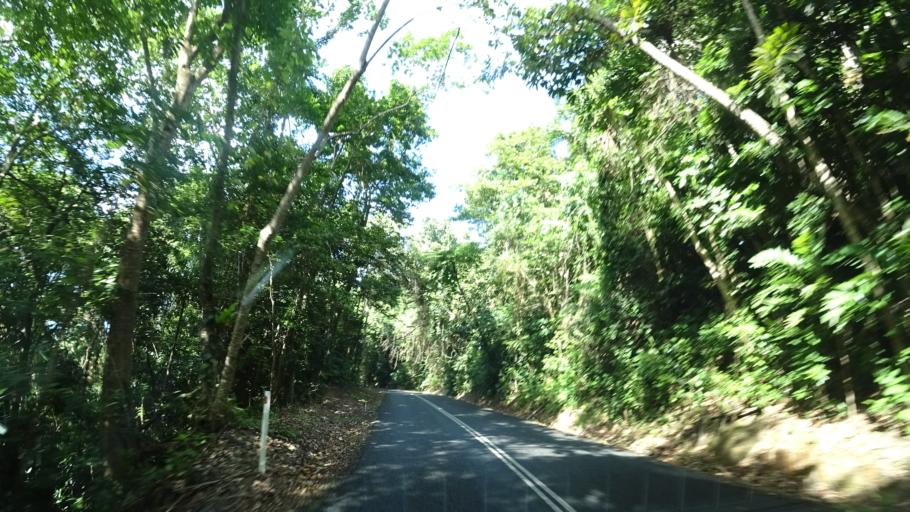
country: AU
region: Queensland
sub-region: Cairns
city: Port Douglas
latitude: -16.1251
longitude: 145.4567
